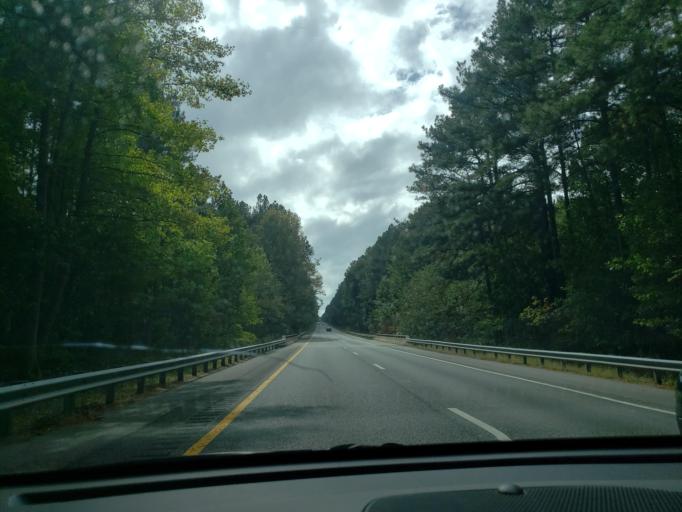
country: US
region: Virginia
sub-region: Brunswick County
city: Lawrenceville
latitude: 36.8821
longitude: -77.8167
